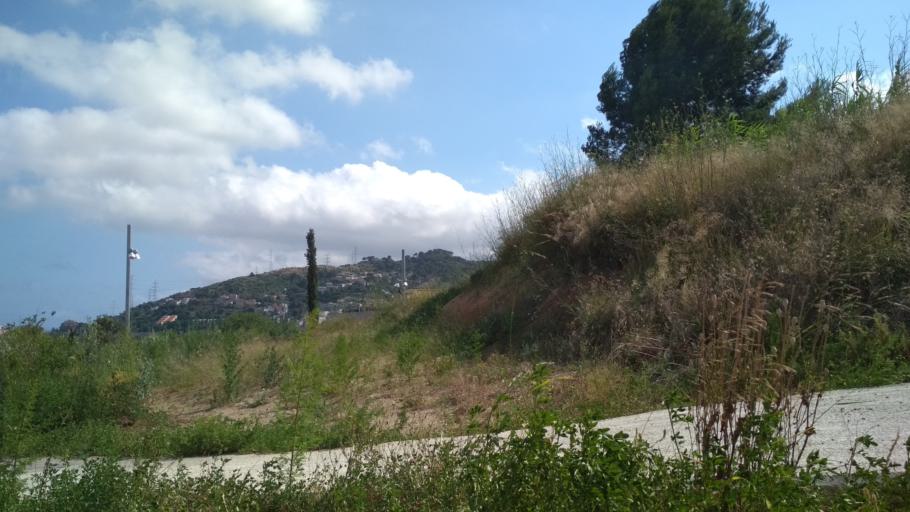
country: ES
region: Catalonia
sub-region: Provincia de Barcelona
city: Montcada i Reixac
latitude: 41.4676
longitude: 2.1863
